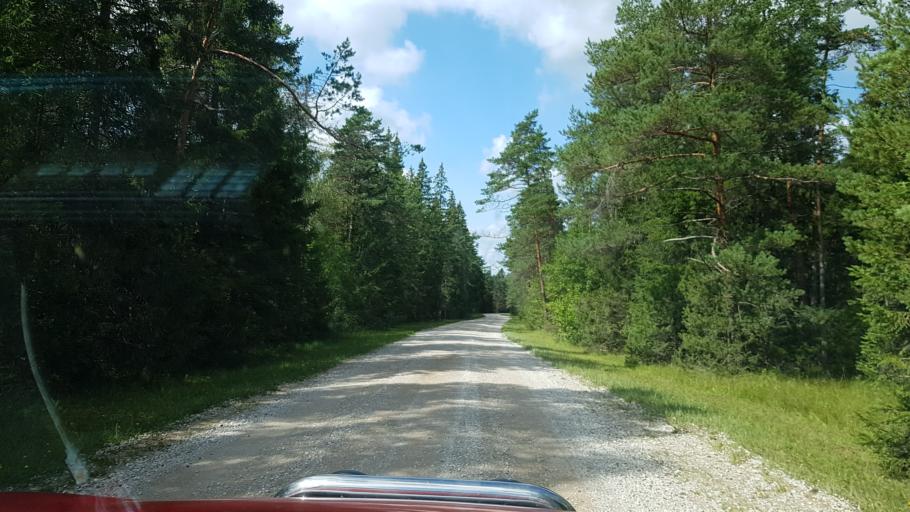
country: EE
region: Raplamaa
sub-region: Rapla vald
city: Rapla
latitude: 58.9582
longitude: 24.6532
